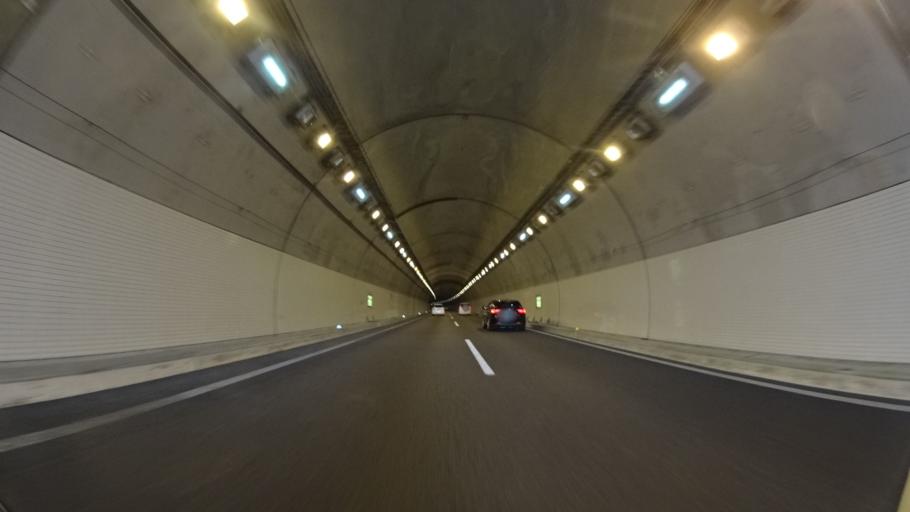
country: JP
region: Ehime
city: Saijo
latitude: 33.9068
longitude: 133.2138
